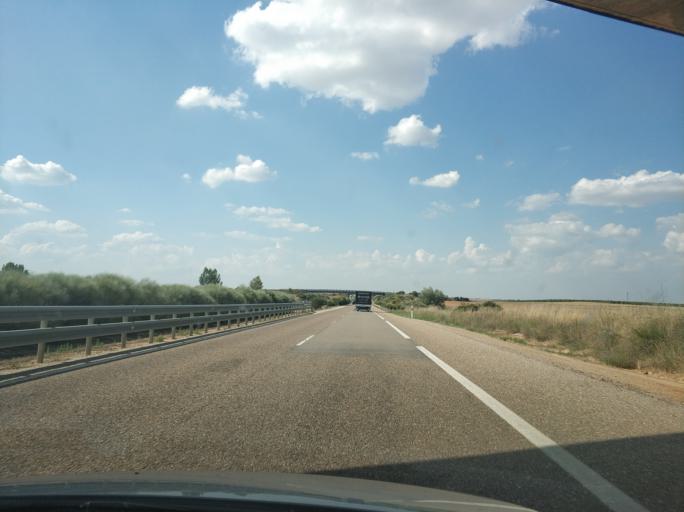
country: ES
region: Castille and Leon
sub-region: Provincia de Zamora
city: Matilla de Arzon
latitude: 42.0899
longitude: -5.6559
